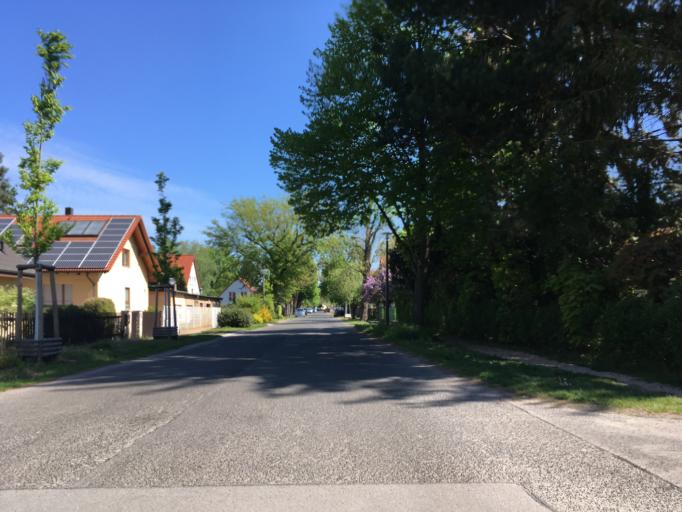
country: DE
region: Berlin
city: Buch
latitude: 52.6464
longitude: 13.5007
